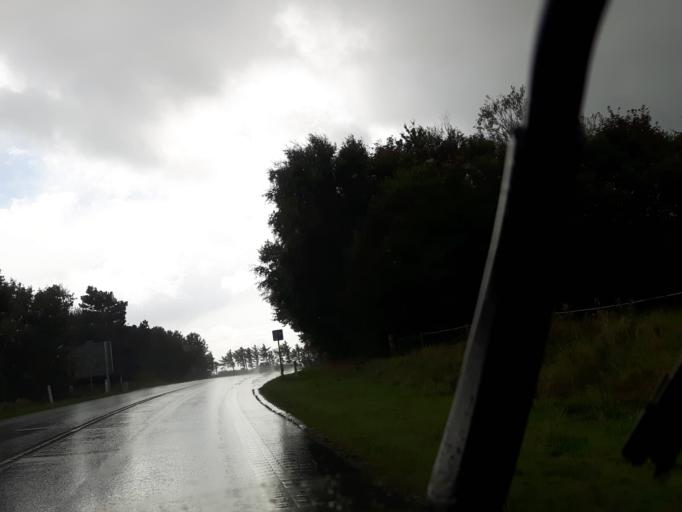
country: DK
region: Central Jutland
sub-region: Struer Kommune
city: Struer
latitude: 56.6056
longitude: 8.5302
